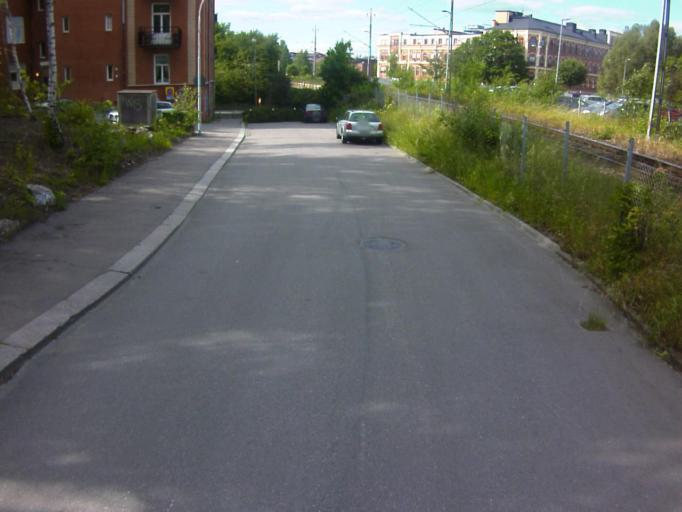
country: SE
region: Soedermanland
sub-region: Eskilstuna Kommun
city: Eskilstuna
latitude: 59.3666
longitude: 16.5112
